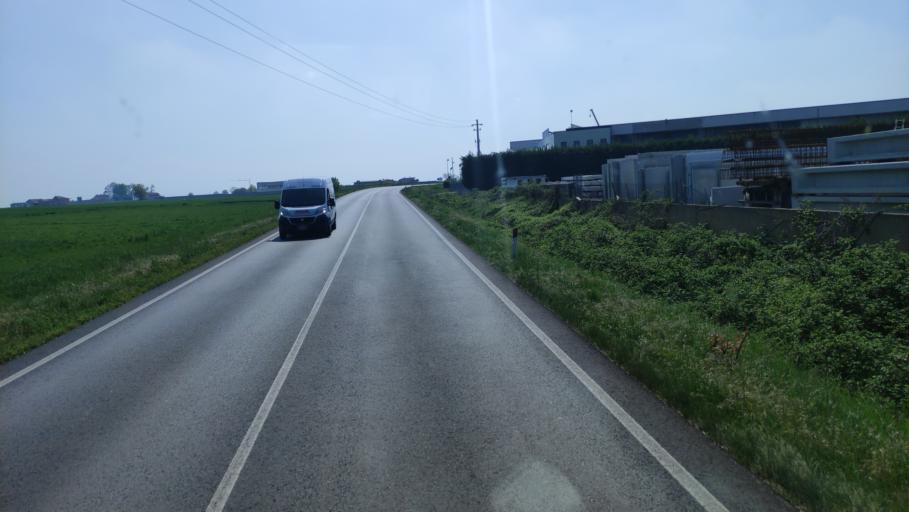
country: IT
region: Piedmont
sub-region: Provincia di Cuneo
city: Marene
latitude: 44.6608
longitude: 7.7465
